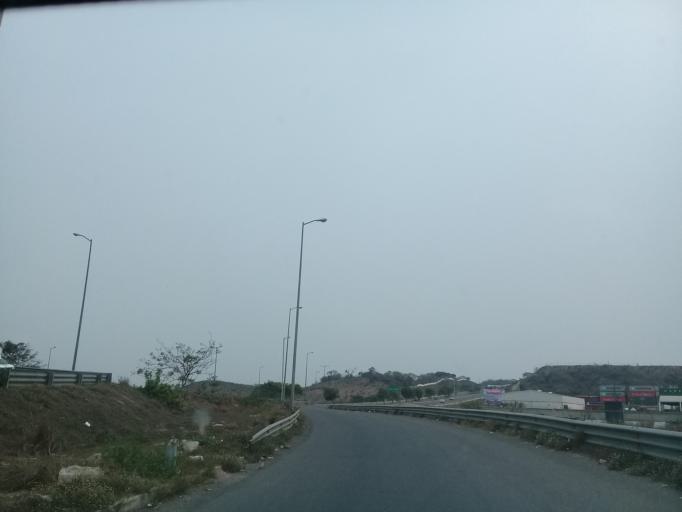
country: MX
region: Veracruz
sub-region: Veracruz
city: Colonia el Renacimiento
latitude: 19.2189
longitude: -96.2195
